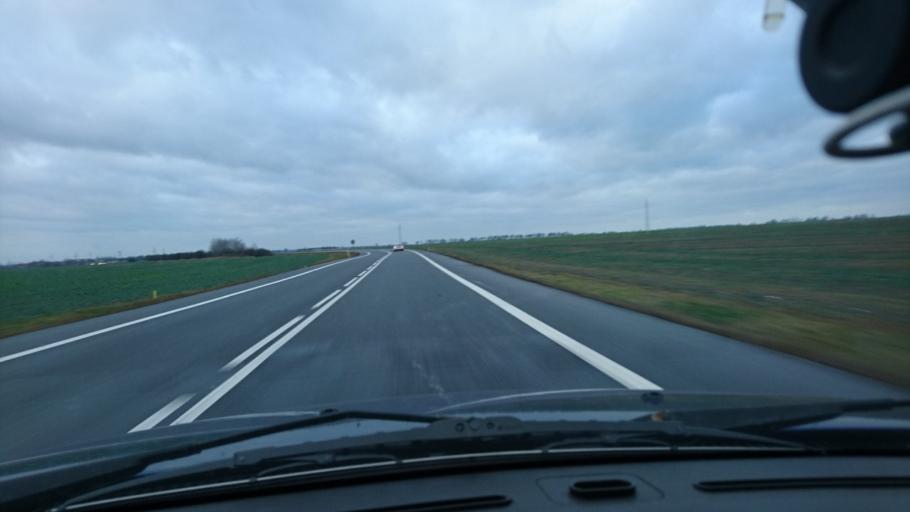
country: PL
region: Opole Voivodeship
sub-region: Powiat kluczborski
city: Kluczbork
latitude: 50.9871
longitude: 18.2372
